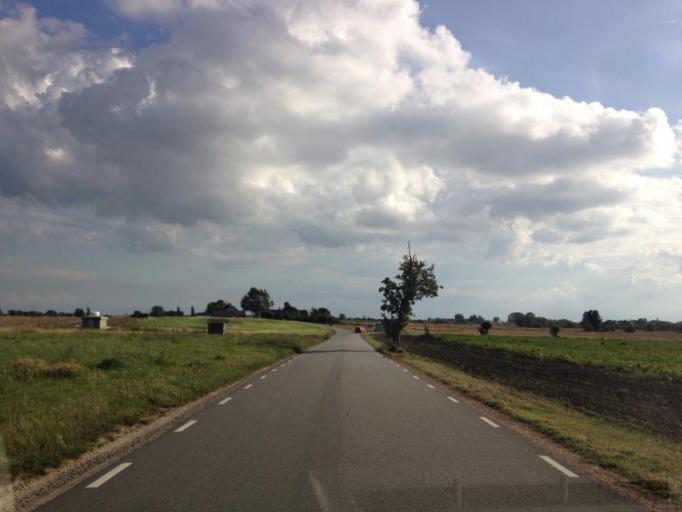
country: SE
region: Skane
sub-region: Trelleborgs Kommun
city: Skare
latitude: 55.4198
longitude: 13.0189
